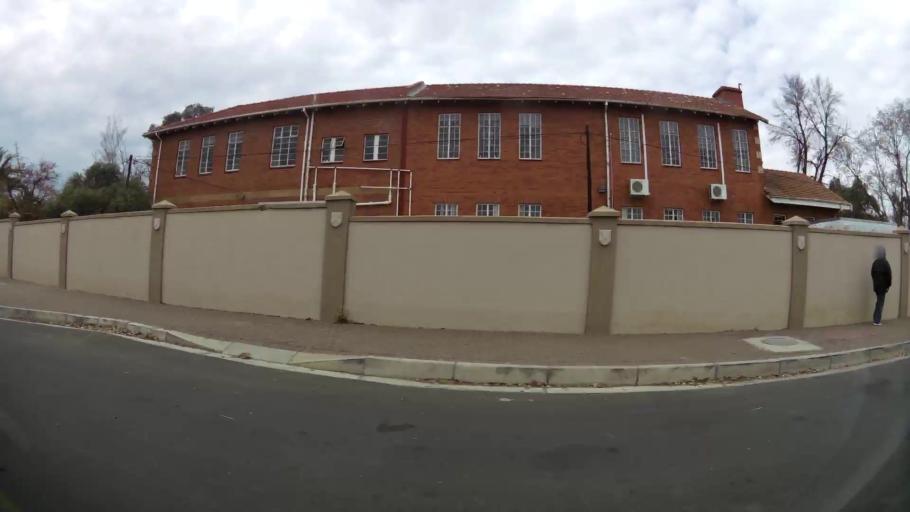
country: ZA
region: Orange Free State
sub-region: Mangaung Metropolitan Municipality
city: Bloemfontein
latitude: -29.1072
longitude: 26.2030
